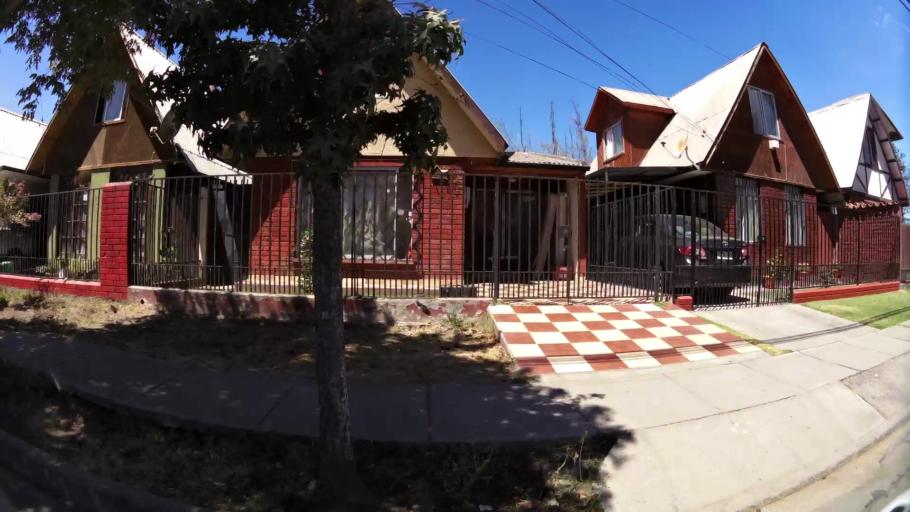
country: CL
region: O'Higgins
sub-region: Provincia de Cachapoal
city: Rancagua
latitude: -34.1654
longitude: -70.7644
